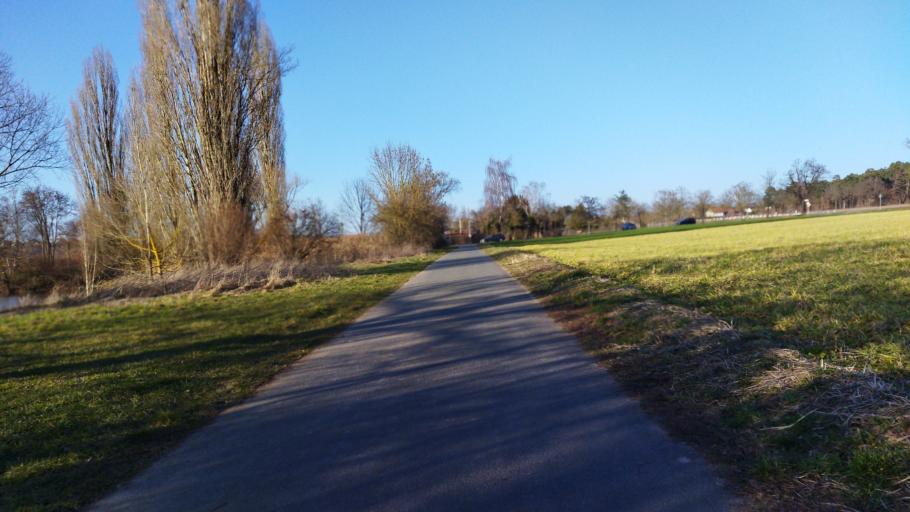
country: DE
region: Bavaria
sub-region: Regierungsbezirk Unterfranken
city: Albertshofen
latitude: 49.7574
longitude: 10.1592
